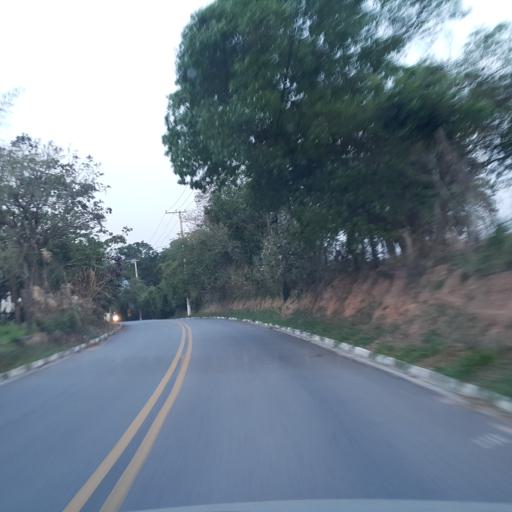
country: BR
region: Sao Paulo
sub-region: Louveira
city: Louveira
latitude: -23.0645
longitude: -46.9676
